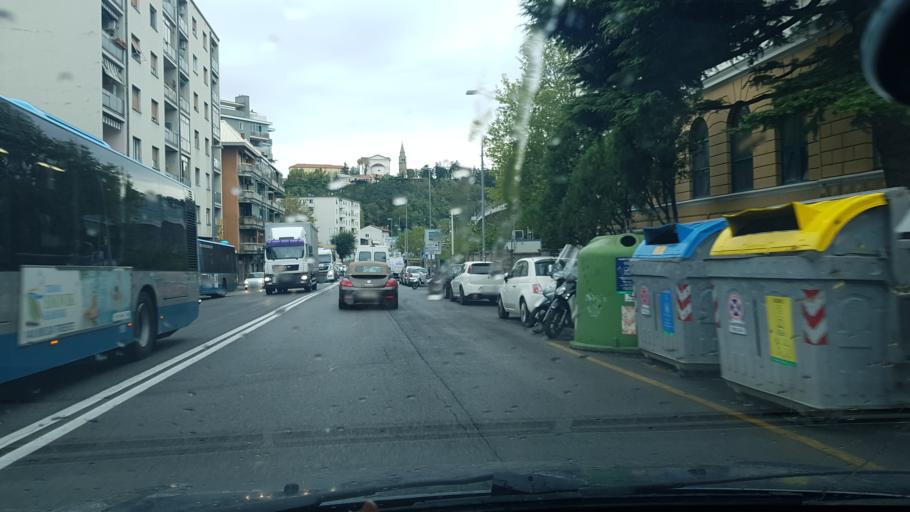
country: IT
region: Friuli Venezia Giulia
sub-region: Provincia di Trieste
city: Trieste
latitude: 45.6304
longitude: 13.7810
